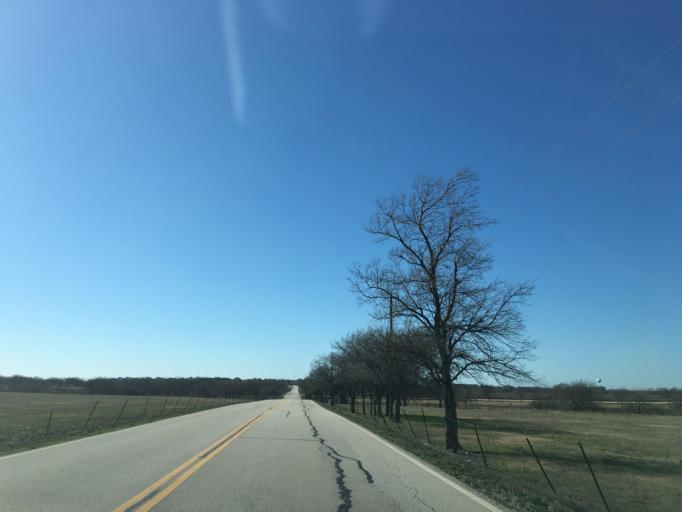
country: US
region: Texas
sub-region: Collin County
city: Prosper
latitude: 33.2330
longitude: -96.8355
